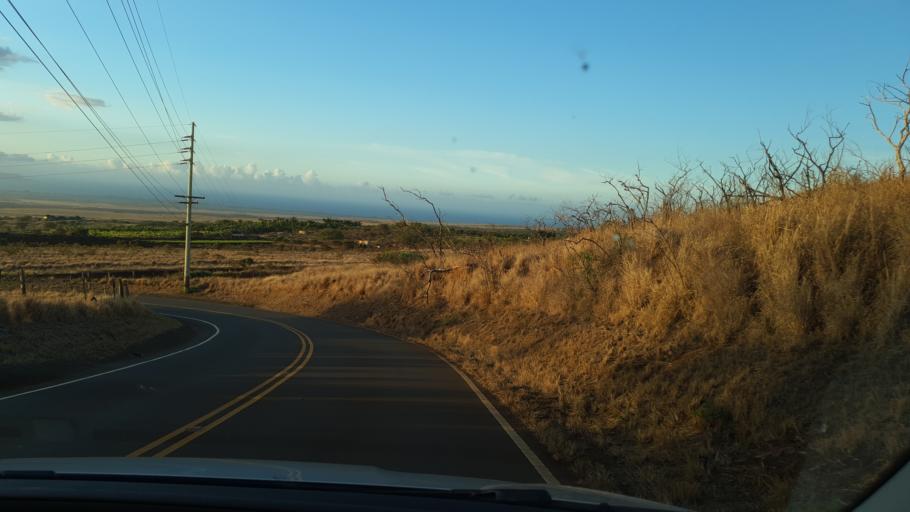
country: US
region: Hawaii
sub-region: Maui County
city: Pukalani
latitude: 20.7920
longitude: -156.3598
